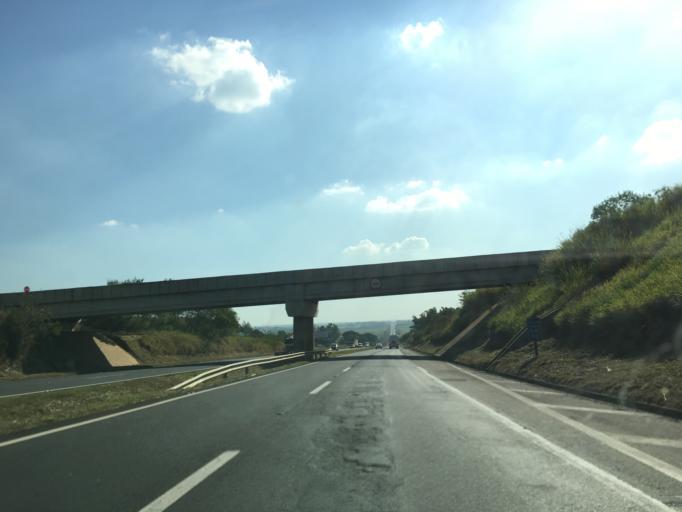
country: BR
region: Sao Paulo
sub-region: Santa Barbara D'Oeste
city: Santa Barbara d'Oeste
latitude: -22.7607
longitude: -47.4612
